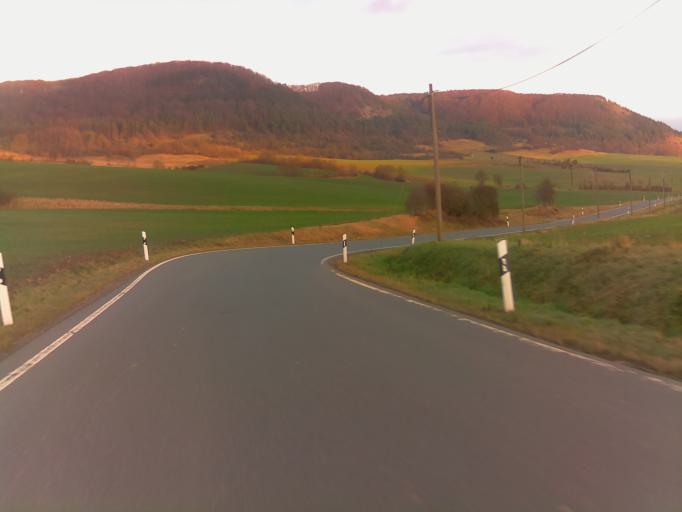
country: DE
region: Thuringia
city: Reinstadt
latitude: 50.7799
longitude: 11.4340
